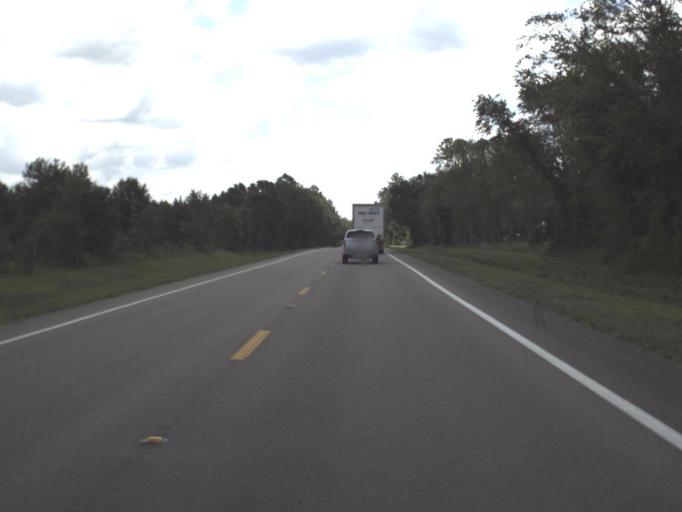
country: US
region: Florida
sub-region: Alachua County
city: Alachua
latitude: 29.8613
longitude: -82.4074
